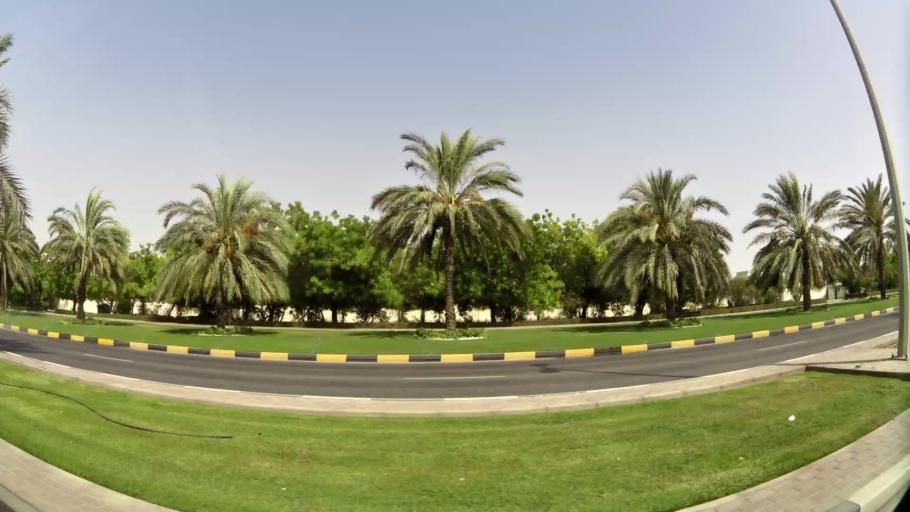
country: AE
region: Ash Shariqah
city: Sharjah
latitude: 25.3321
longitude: 55.4378
